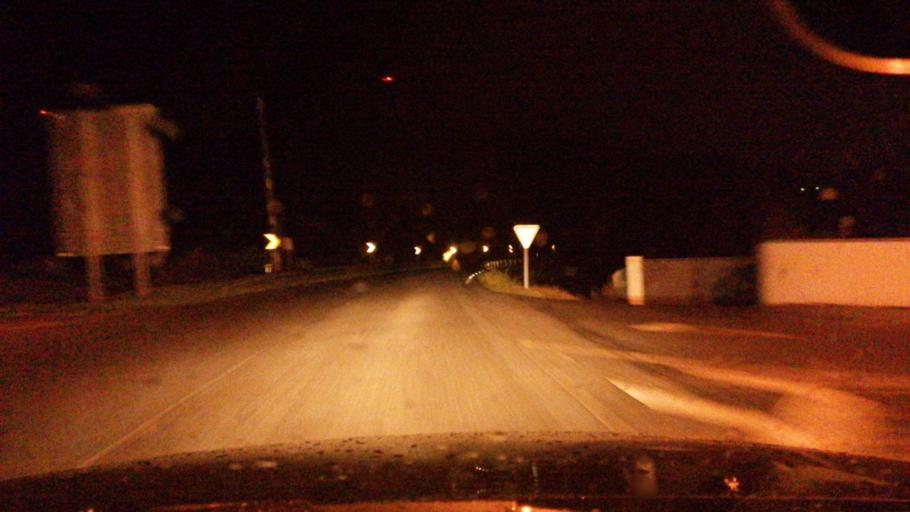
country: PT
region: Viseu
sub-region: Moimenta da Beira
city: Moimenta da Beira
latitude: 40.9578
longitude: -7.5853
